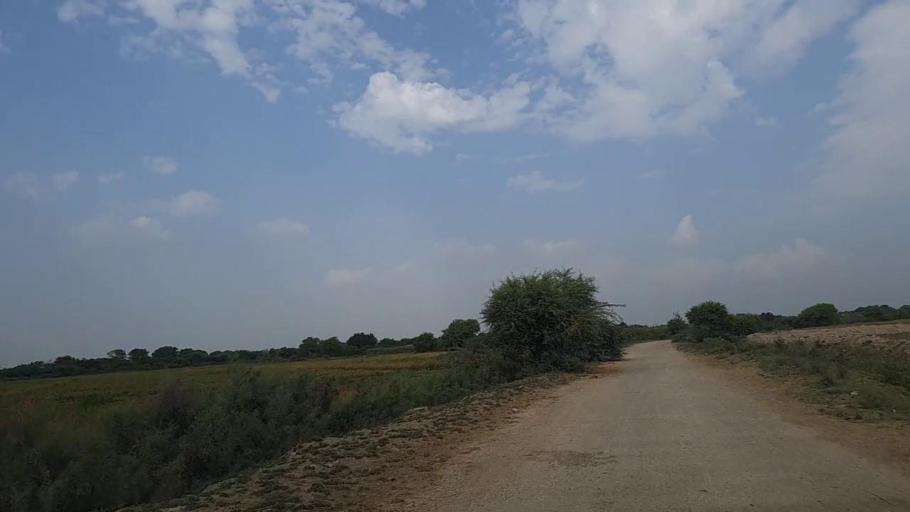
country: PK
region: Sindh
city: Daro Mehar
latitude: 24.7123
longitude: 68.1529
